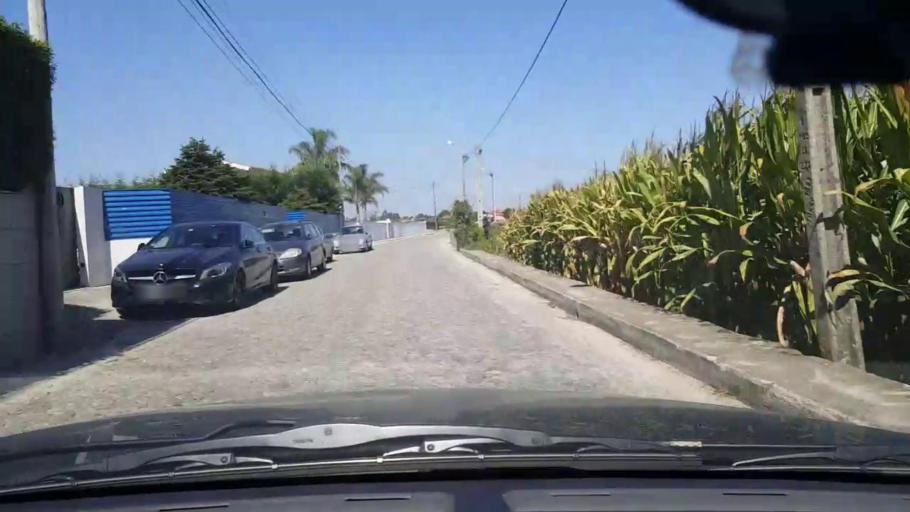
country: PT
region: Porto
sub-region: Matosinhos
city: Lavra
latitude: 41.2638
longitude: -8.6963
